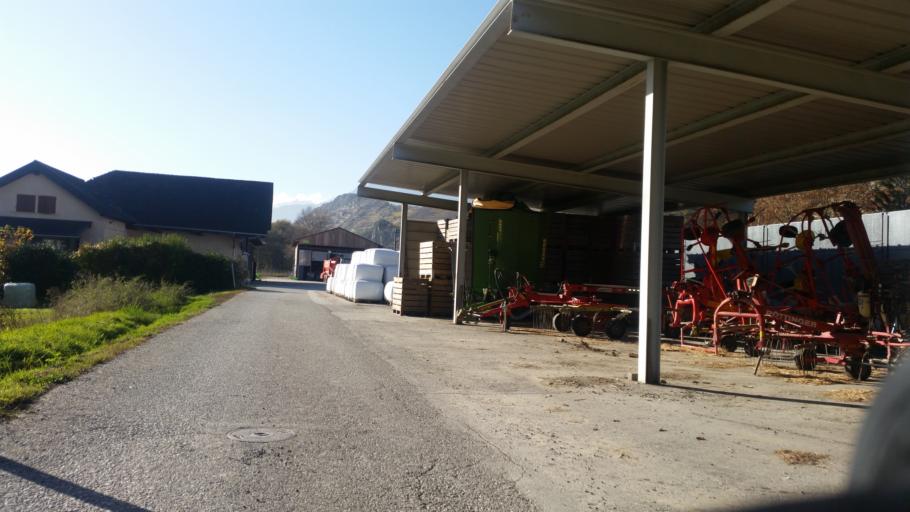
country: CH
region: Valais
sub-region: Sion District
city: Saint-Leonard
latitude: 46.2491
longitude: 7.4091
